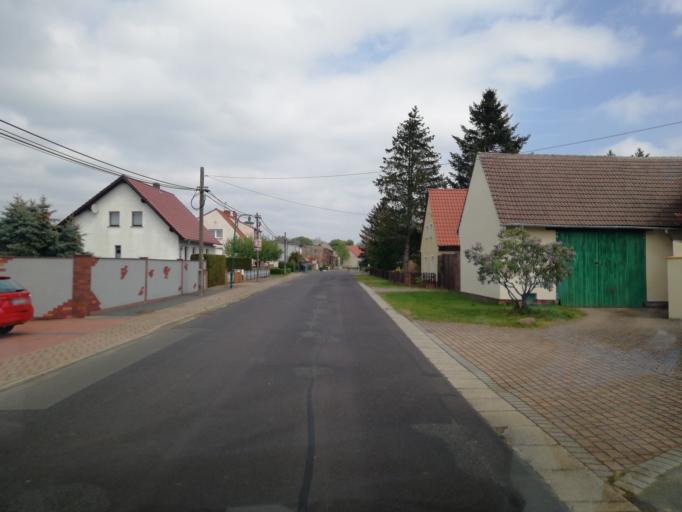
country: DE
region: Brandenburg
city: Hohenbucko
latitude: 51.6968
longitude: 13.4626
